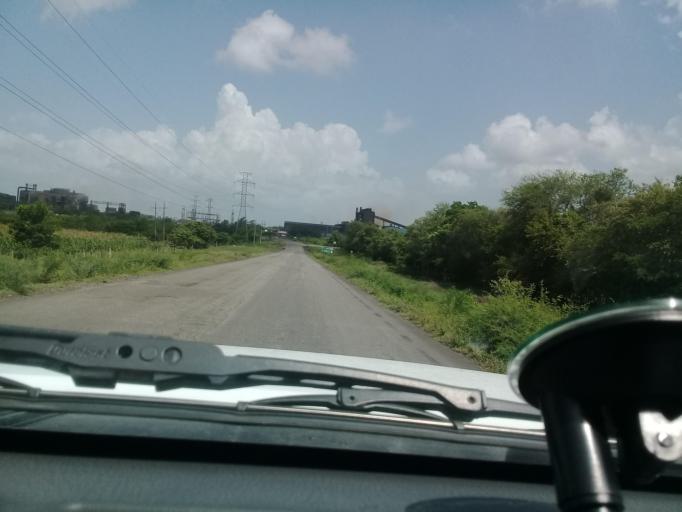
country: MX
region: Veracruz
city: Moralillo
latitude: 22.2297
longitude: -98.0170
